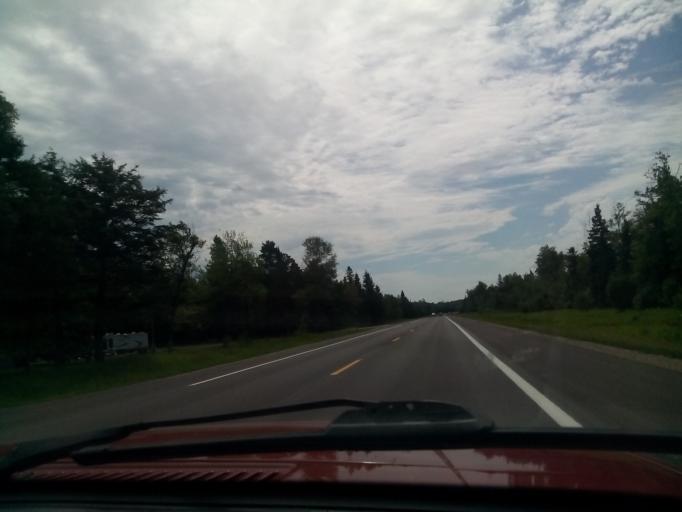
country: US
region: Michigan
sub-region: Schoolcraft County
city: Manistique
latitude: 46.0684
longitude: -85.9584
